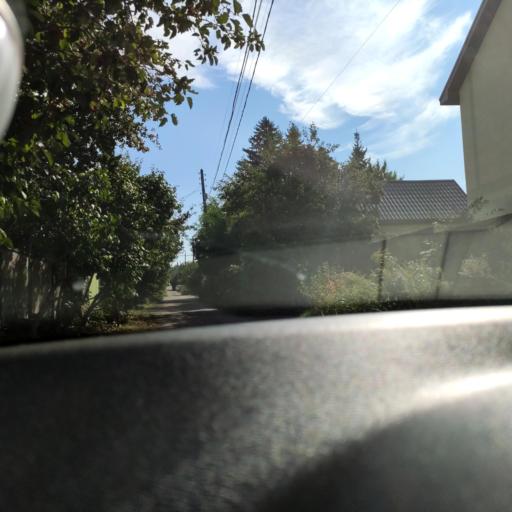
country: RU
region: Samara
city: Samara
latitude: 53.2940
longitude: 50.2141
